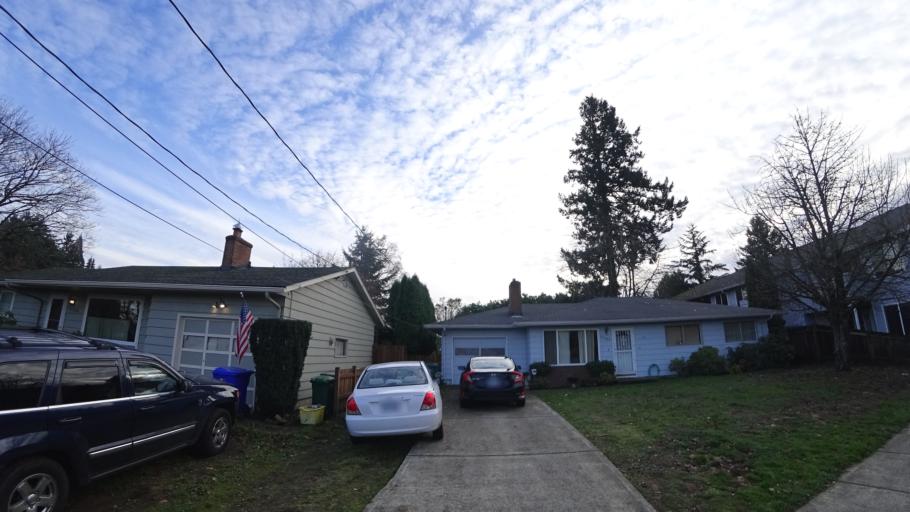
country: US
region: Oregon
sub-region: Multnomah County
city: Lents
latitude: 45.5167
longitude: -122.5324
